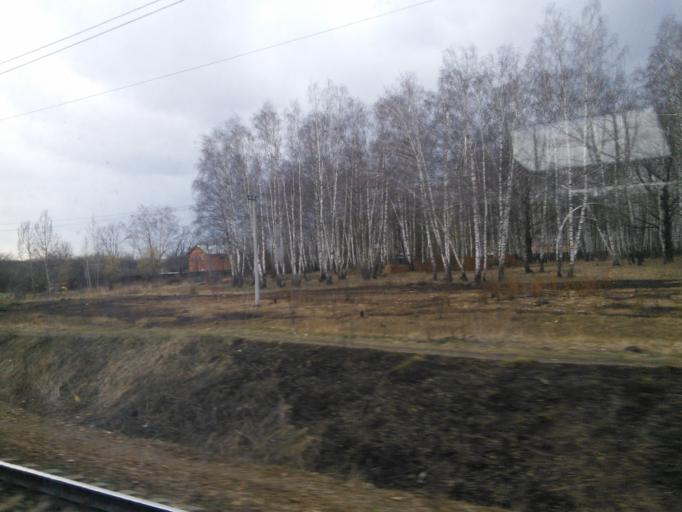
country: RU
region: Moskovskaya
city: Klimovsk
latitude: 55.3831
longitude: 37.5330
